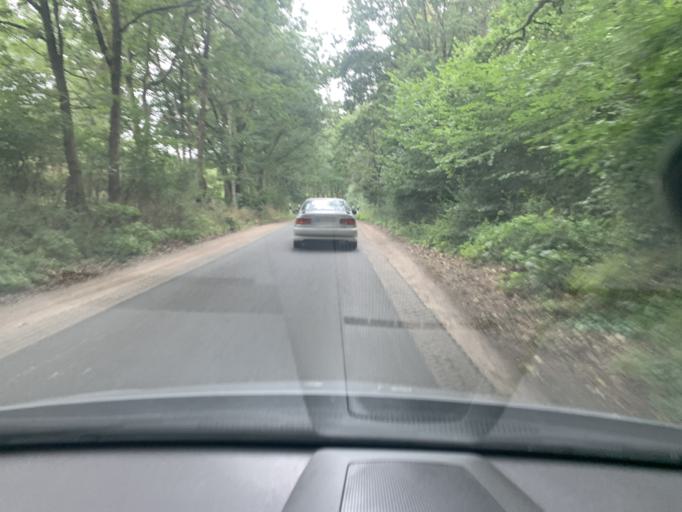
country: DE
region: Schleswig-Holstein
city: Grambek
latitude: 53.5637
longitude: 10.6870
